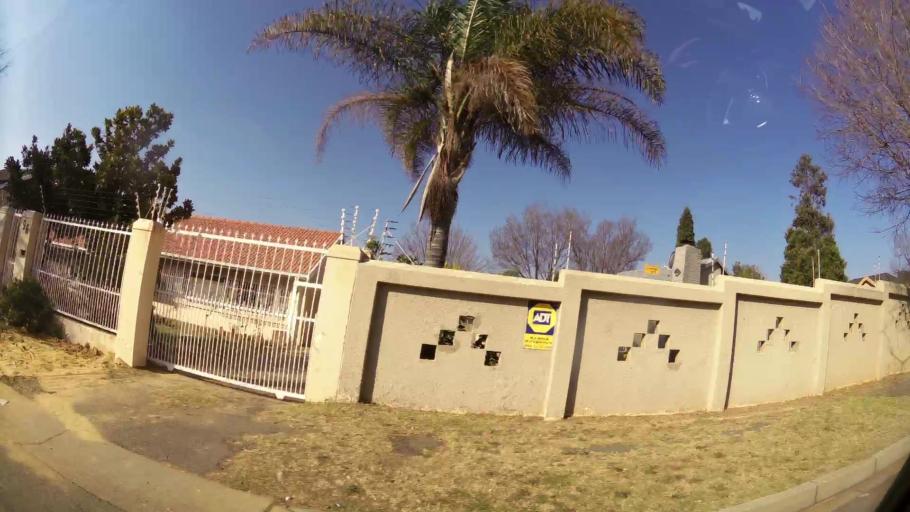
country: ZA
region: Gauteng
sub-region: City of Johannesburg Metropolitan Municipality
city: Johannesburg
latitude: -26.2462
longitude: 28.0079
